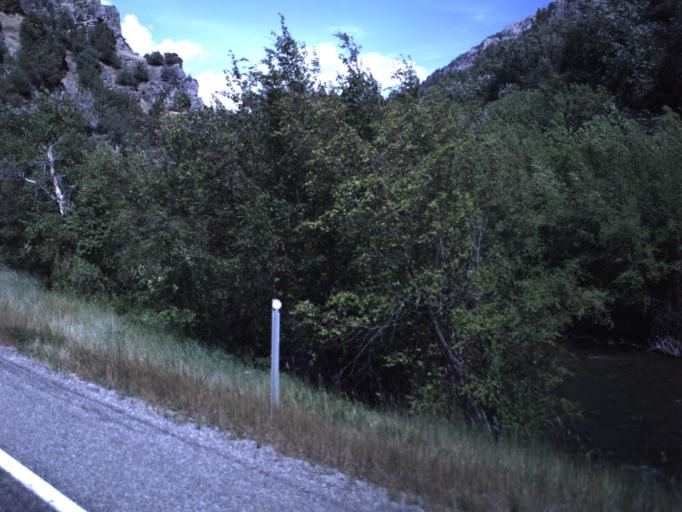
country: US
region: Utah
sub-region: Cache County
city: North Logan
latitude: 41.7664
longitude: -111.6668
